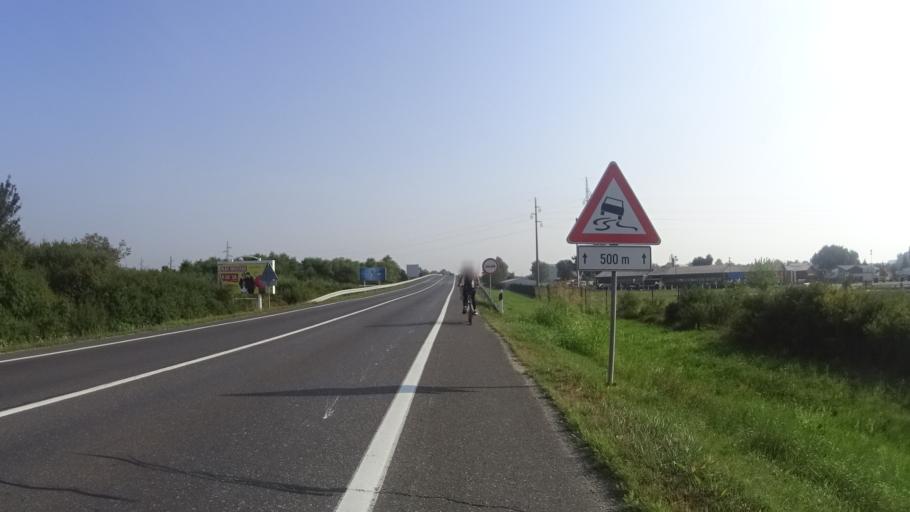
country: HR
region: Medimurska
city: Nedelisce
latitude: 46.3823
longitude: 16.4029
